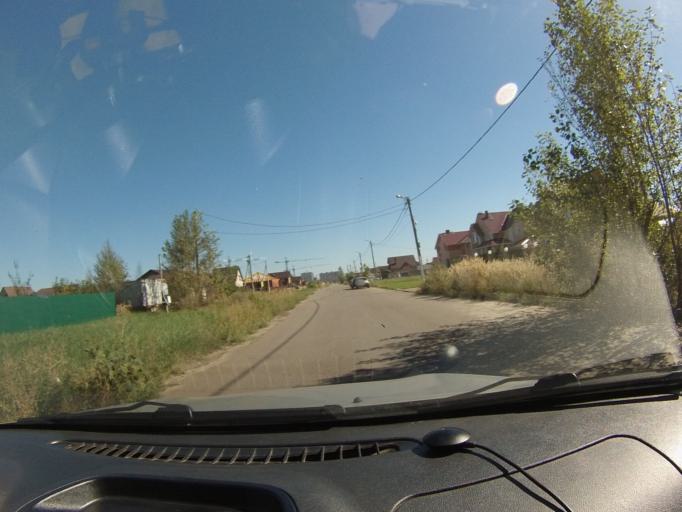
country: RU
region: Tambov
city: Tambov
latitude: 52.7723
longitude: 41.3762
